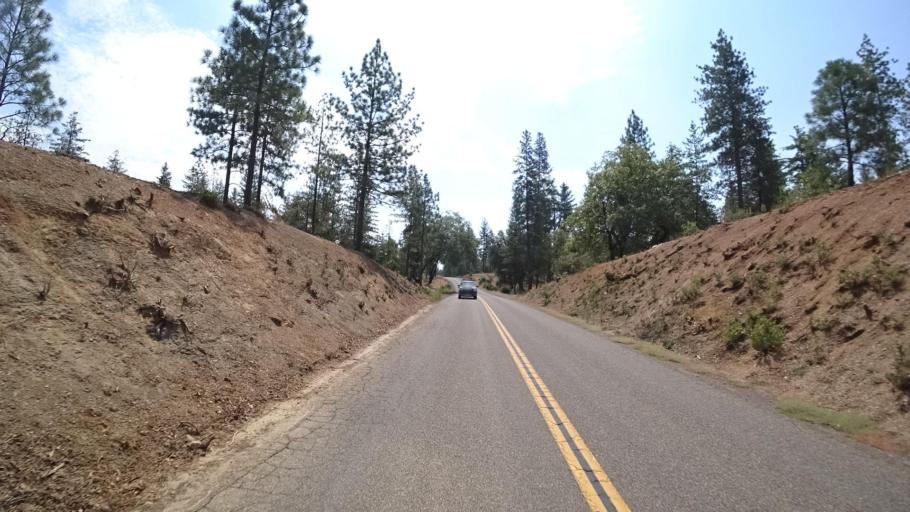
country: US
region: California
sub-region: Tuolumne County
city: Tuolumne City
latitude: 37.7308
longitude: -120.1189
